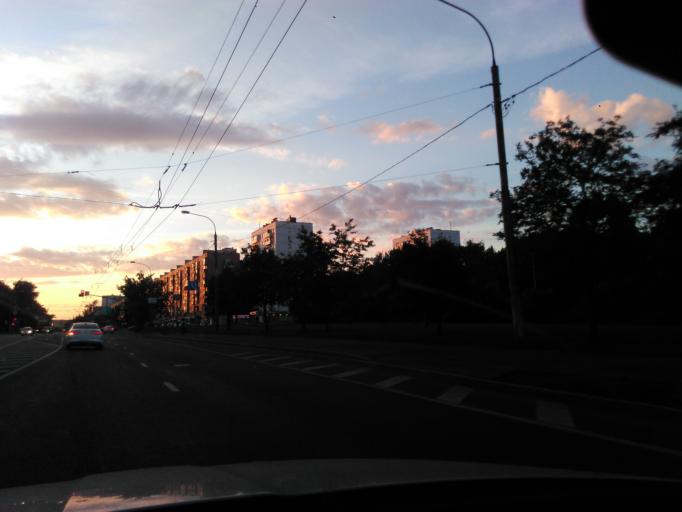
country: RU
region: Moscow
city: Zapadnoye Degunino
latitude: 55.8772
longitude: 37.5241
